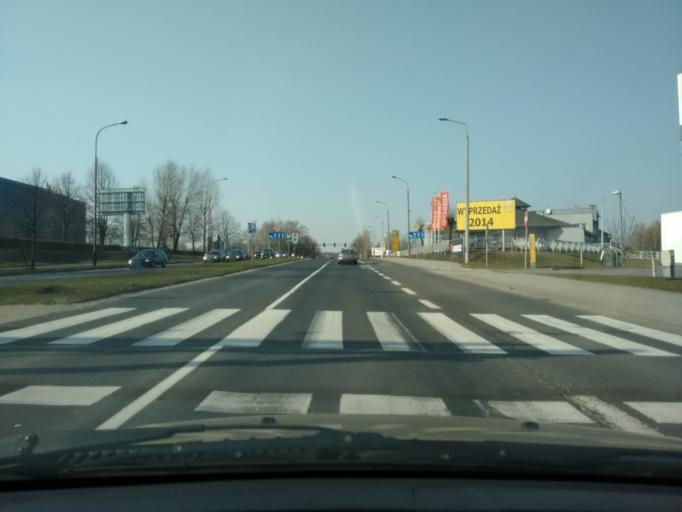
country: PL
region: Silesian Voivodeship
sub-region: Bielsko-Biala
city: Bielsko-Biala
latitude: 49.8419
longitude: 19.0360
